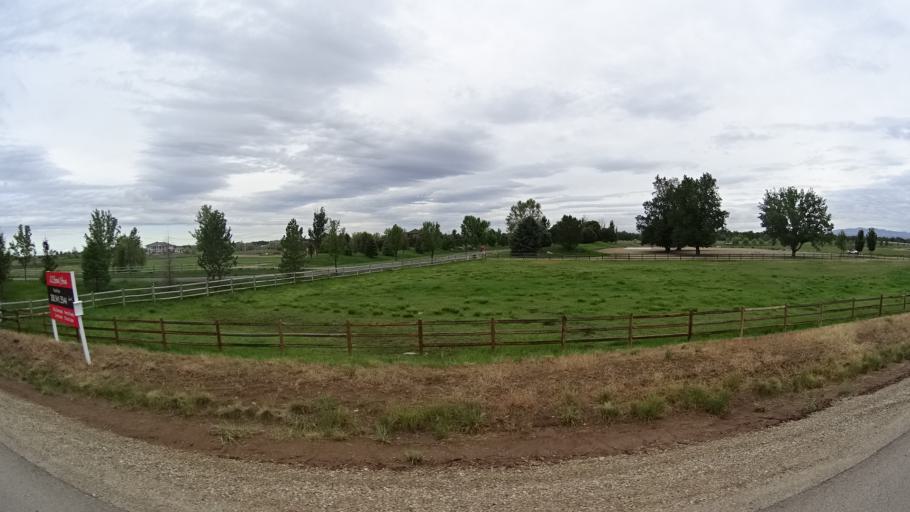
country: US
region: Idaho
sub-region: Ada County
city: Star
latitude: 43.6701
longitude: -116.4727
